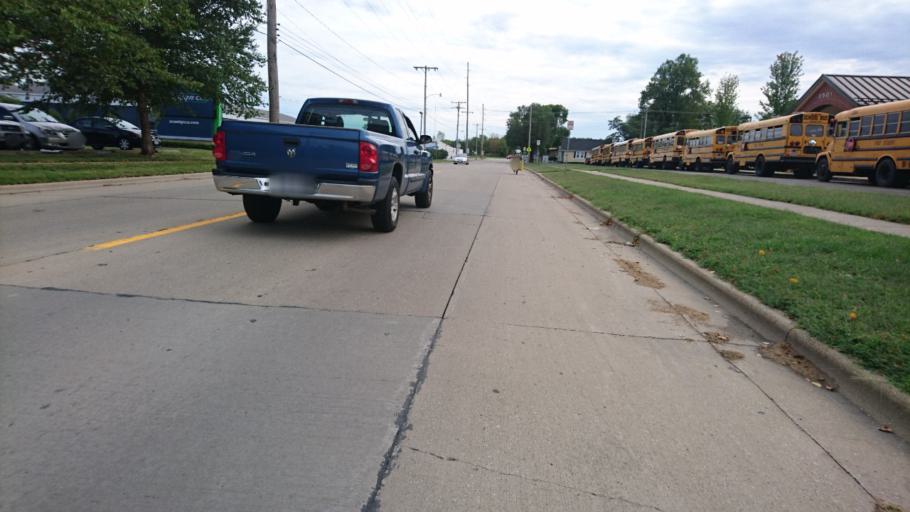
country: US
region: Illinois
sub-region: Sangamon County
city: Southern View
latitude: 39.7730
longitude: -89.6543
